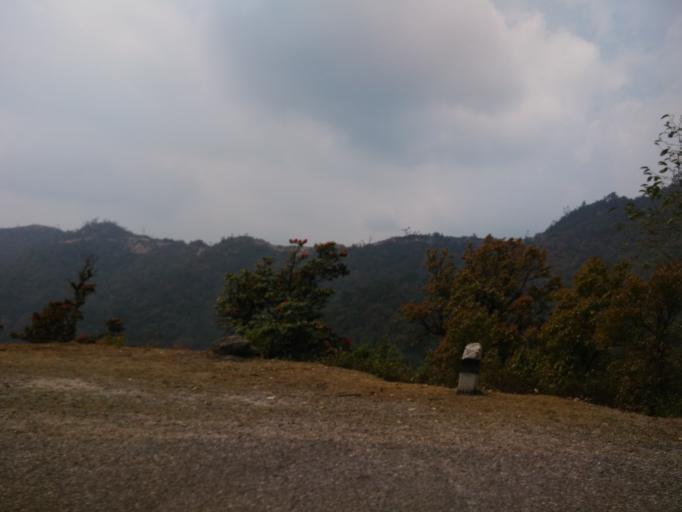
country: NP
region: Central Region
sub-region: Narayani Zone
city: Hitura
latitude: 27.5701
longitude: 85.0747
